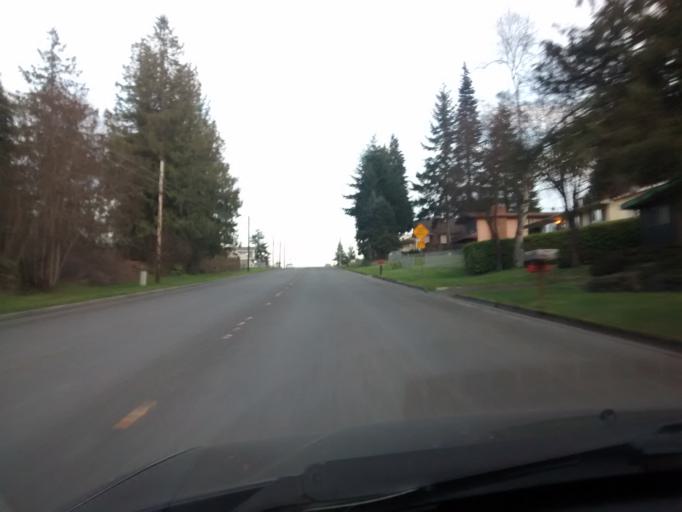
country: US
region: Washington
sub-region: Clallam County
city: Port Angeles
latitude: 48.1226
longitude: -123.4629
